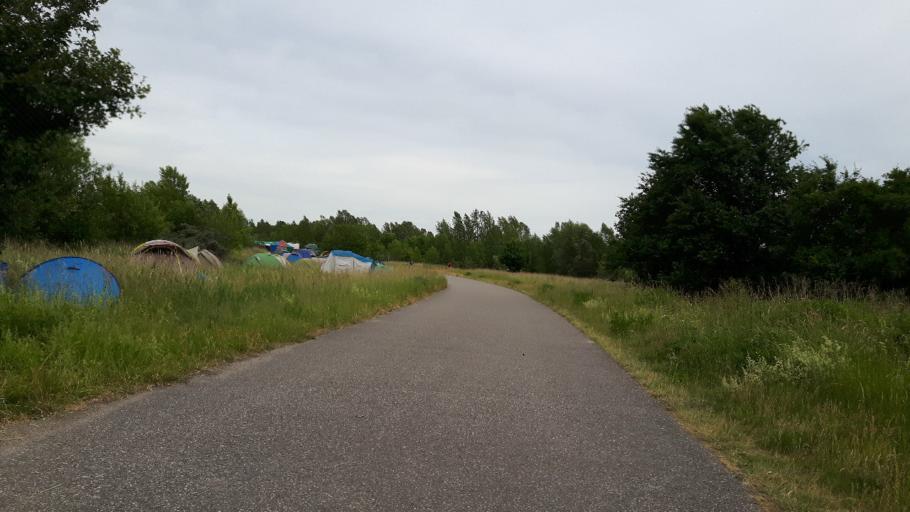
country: DE
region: Saxony
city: Zwochau
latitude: 51.4298
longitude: 12.3202
